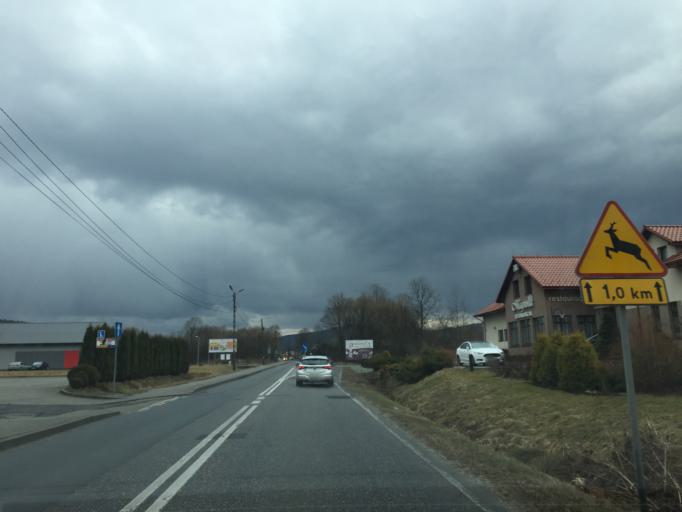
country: PL
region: Lesser Poland Voivodeship
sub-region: Powiat suski
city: Budzow
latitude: 49.7710
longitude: 19.6461
